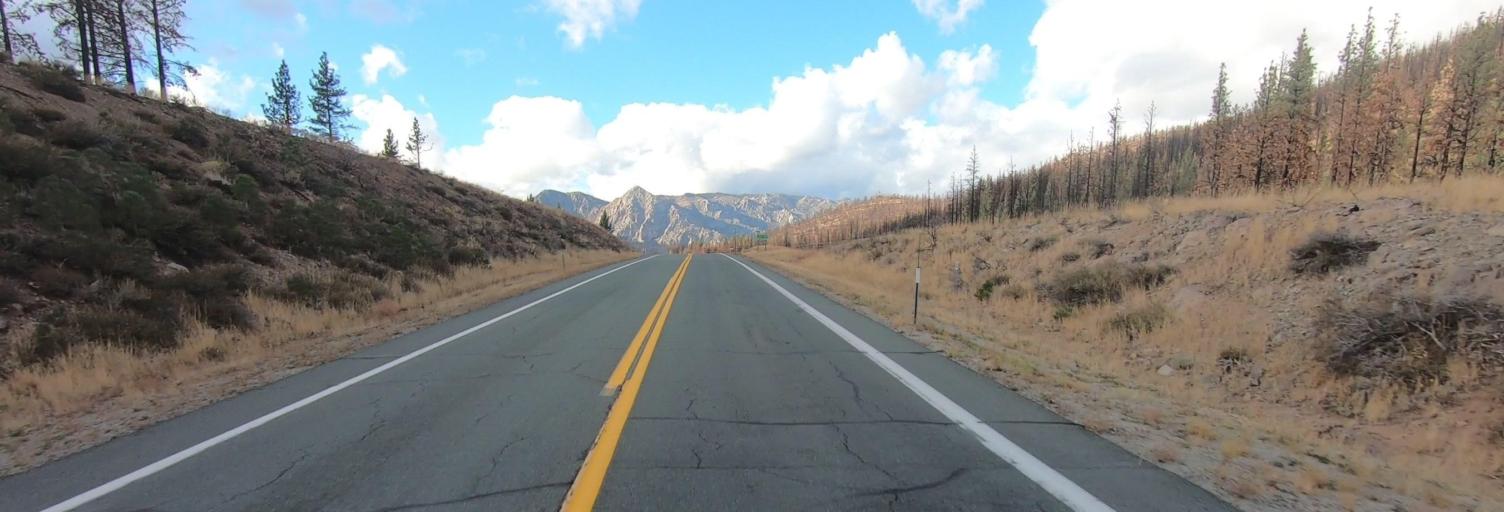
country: US
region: Nevada
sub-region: Douglas County
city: Gardnerville Ranchos
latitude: 38.7225
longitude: -119.7983
